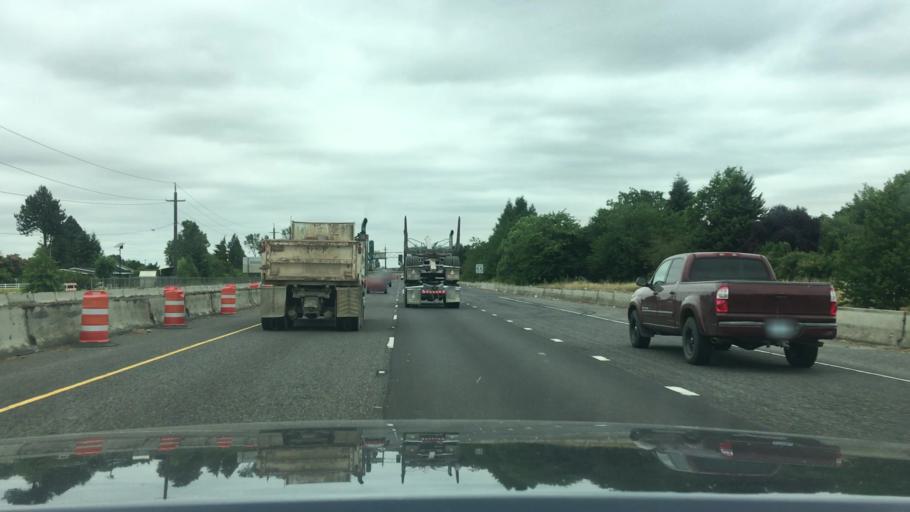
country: US
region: Oregon
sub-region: Lane County
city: Eugene
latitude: 44.0905
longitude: -123.1711
